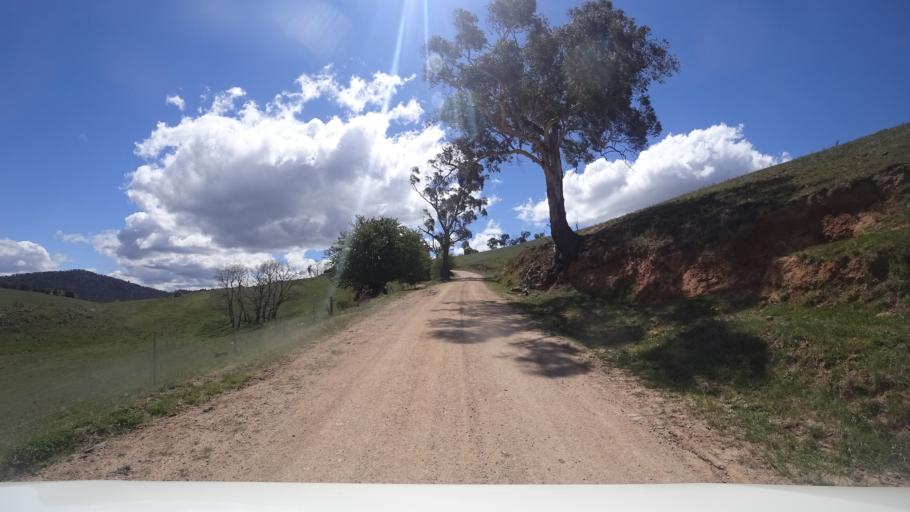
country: AU
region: New South Wales
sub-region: Oberon
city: Oberon
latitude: -33.5748
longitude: 149.9413
